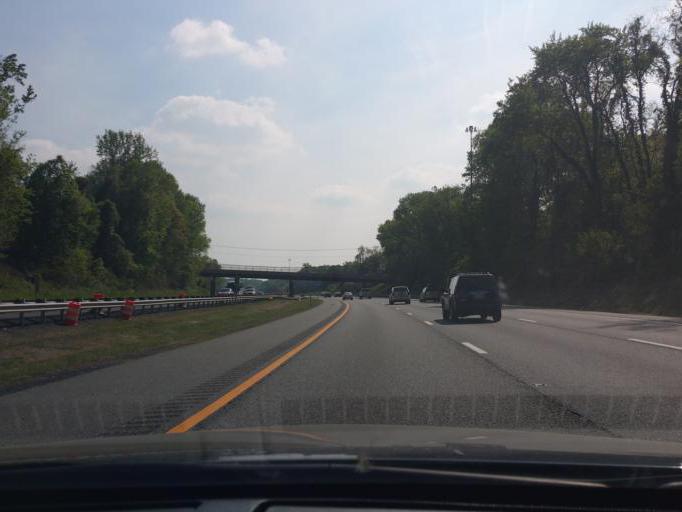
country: US
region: Maryland
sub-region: Harford County
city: Havre de Grace
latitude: 39.5731
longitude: -76.1359
